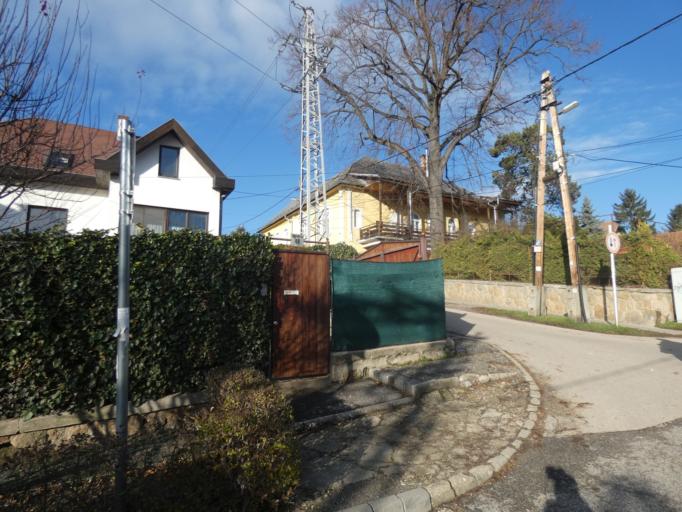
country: HU
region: Pest
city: Budakeszi
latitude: 47.5155
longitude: 18.9401
